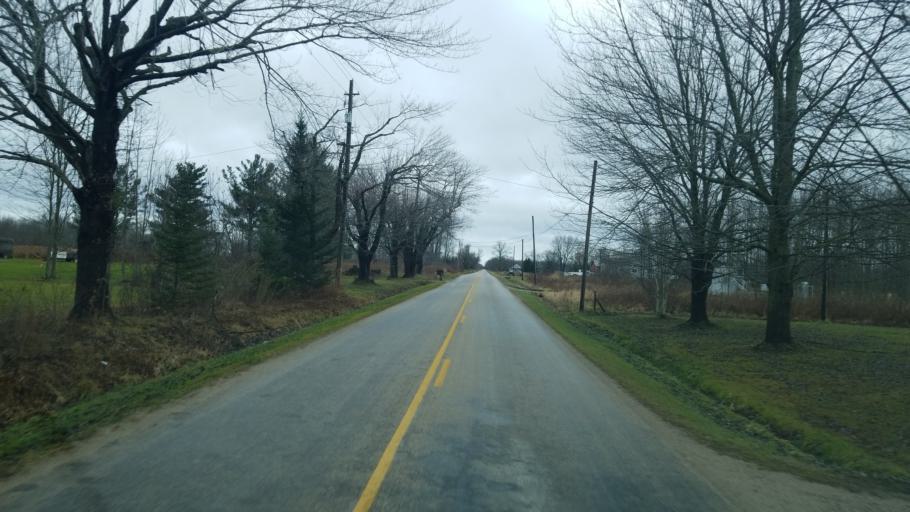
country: US
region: Ohio
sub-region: Ashtabula County
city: North Kingsville
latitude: 41.7848
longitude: -80.6236
